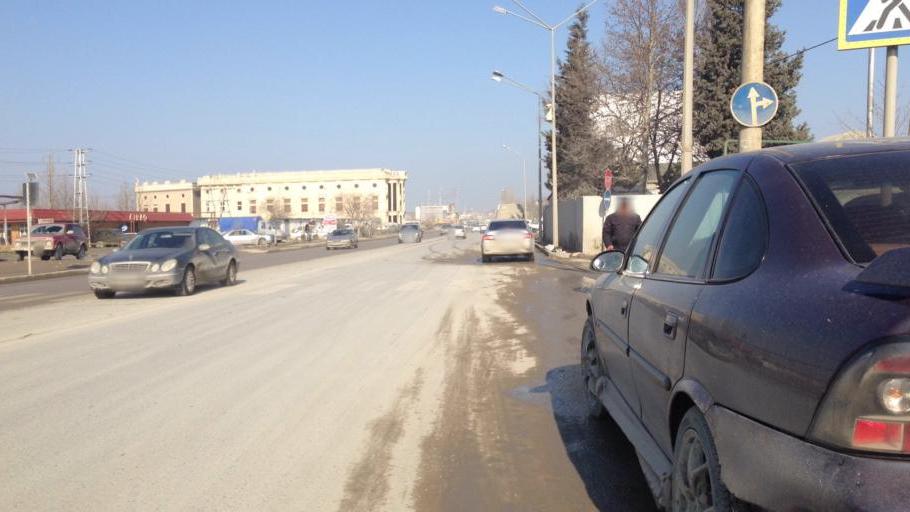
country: AZ
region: Baki
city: Binagadi
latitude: 40.4433
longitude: 49.8446
